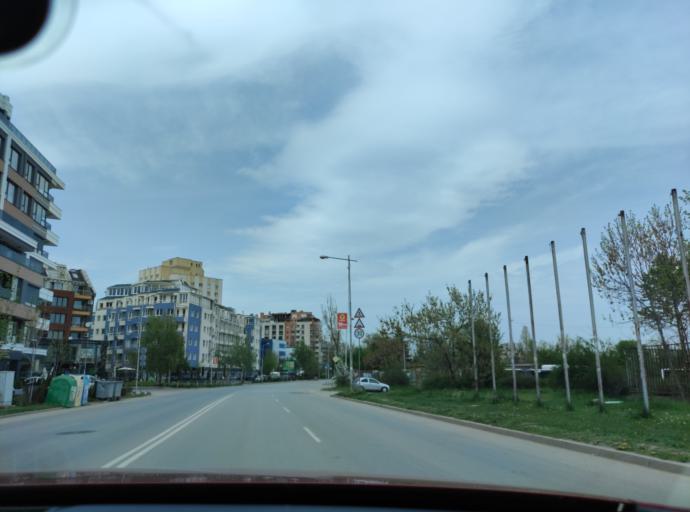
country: BG
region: Sofia-Capital
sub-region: Stolichna Obshtina
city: Sofia
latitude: 42.6463
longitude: 23.3453
